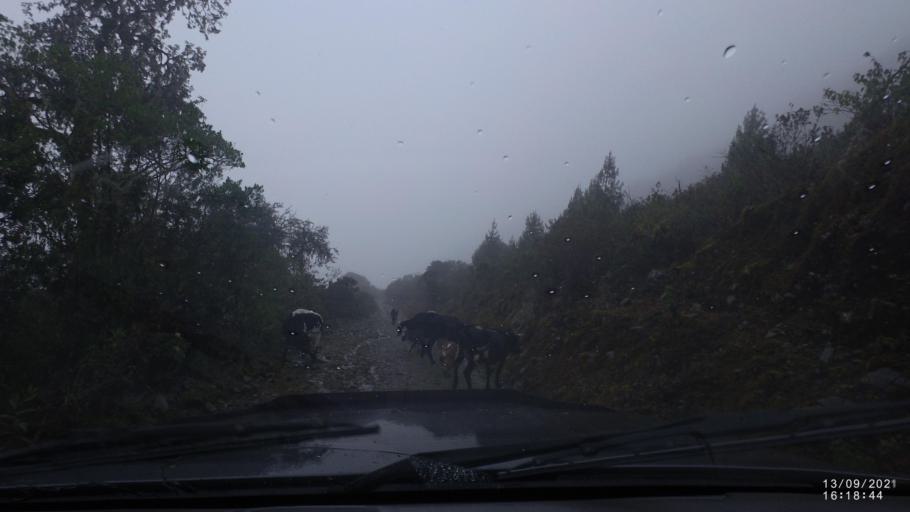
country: BO
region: Cochabamba
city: Colomi
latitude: -17.2703
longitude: -65.7059
